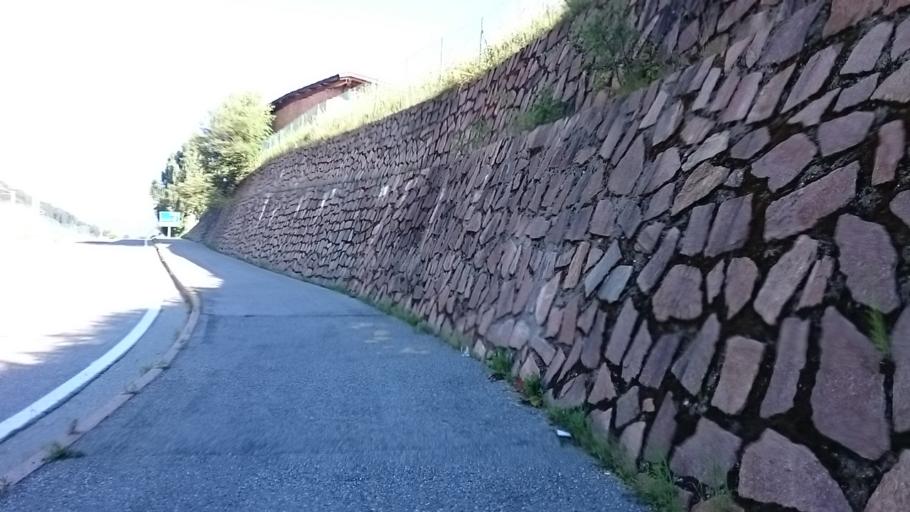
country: IT
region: Trentino-Alto Adige
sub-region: Bolzano
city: Monguelfo
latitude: 46.7538
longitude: 12.1035
